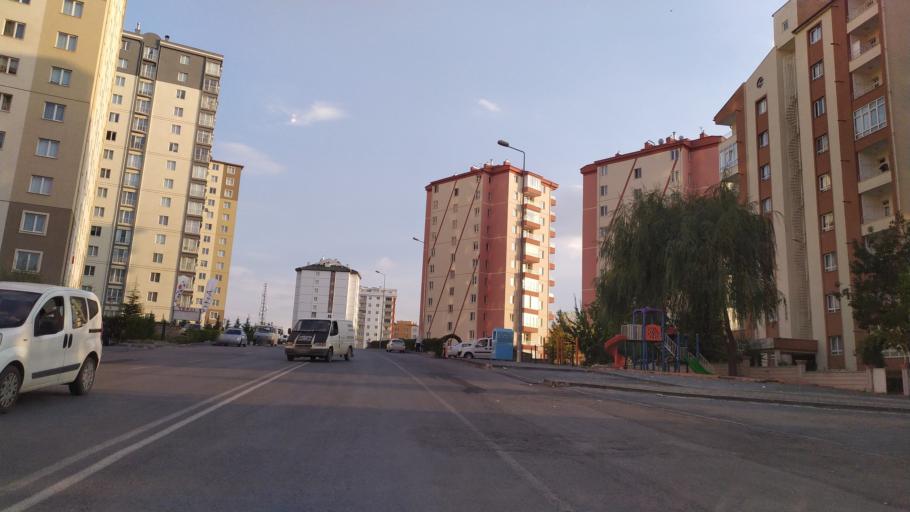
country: TR
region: Kayseri
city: Talas
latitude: 38.7013
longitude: 35.5635
